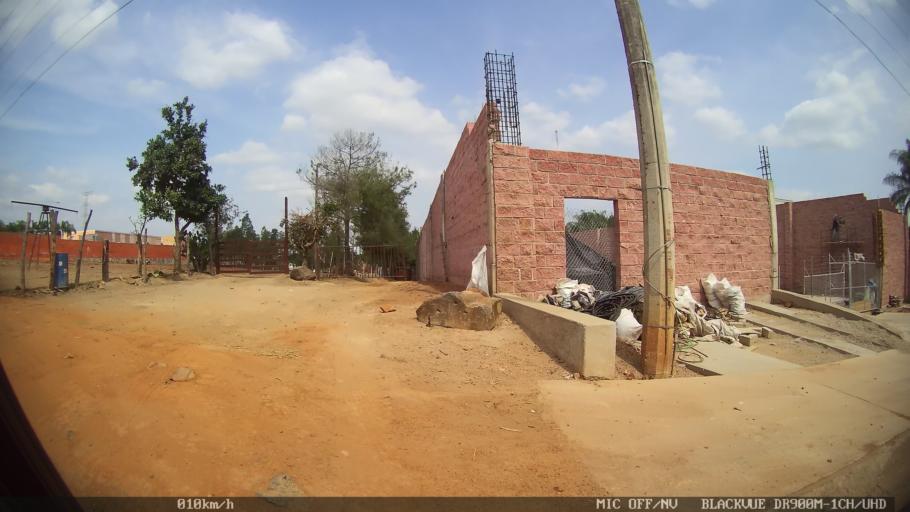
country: MX
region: Jalisco
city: Tonala
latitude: 20.6455
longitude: -103.2220
